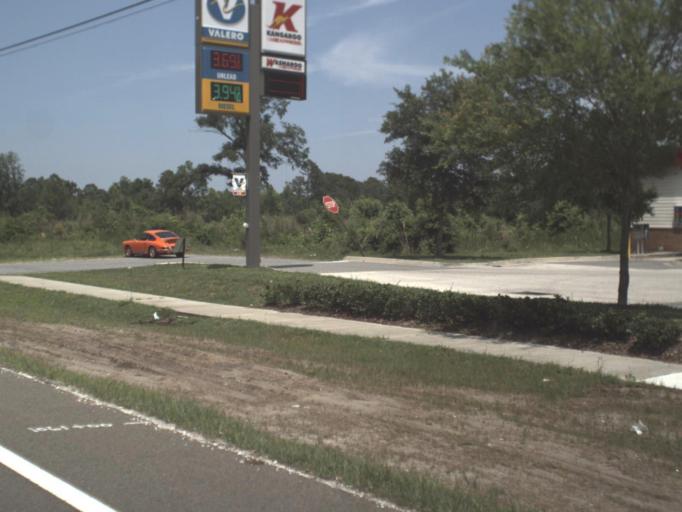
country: US
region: Florida
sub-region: Nassau County
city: Yulee
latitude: 30.4909
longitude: -81.6248
